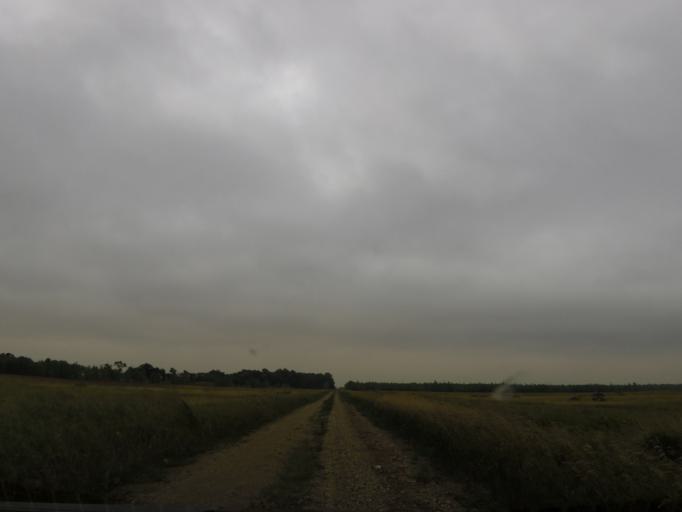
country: US
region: North Dakota
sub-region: Walsh County
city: Grafton
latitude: 48.4277
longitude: -97.1268
